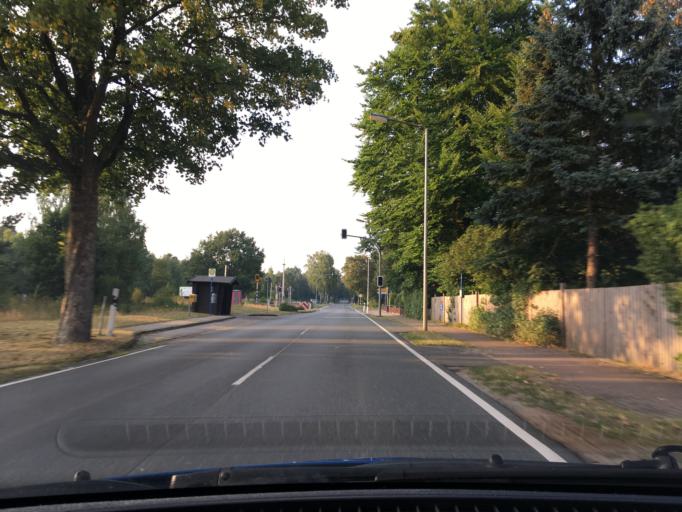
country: DE
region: Lower Saxony
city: Celle
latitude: 52.7054
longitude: 10.0802
